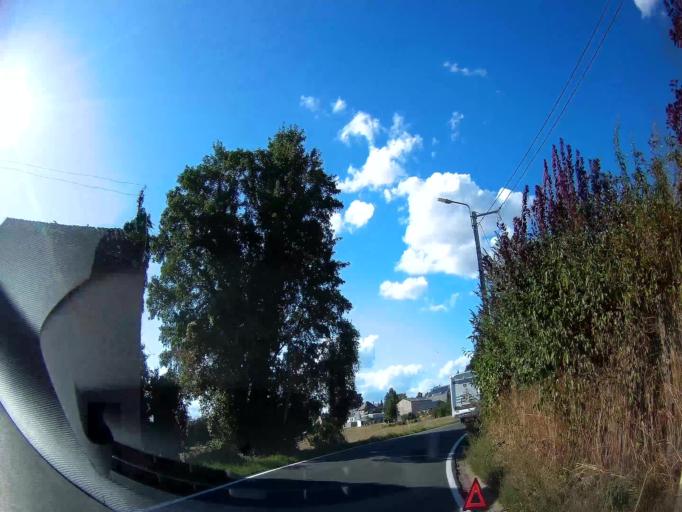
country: BE
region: Wallonia
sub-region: Province de Namur
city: Mettet
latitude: 50.3163
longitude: 4.7565
